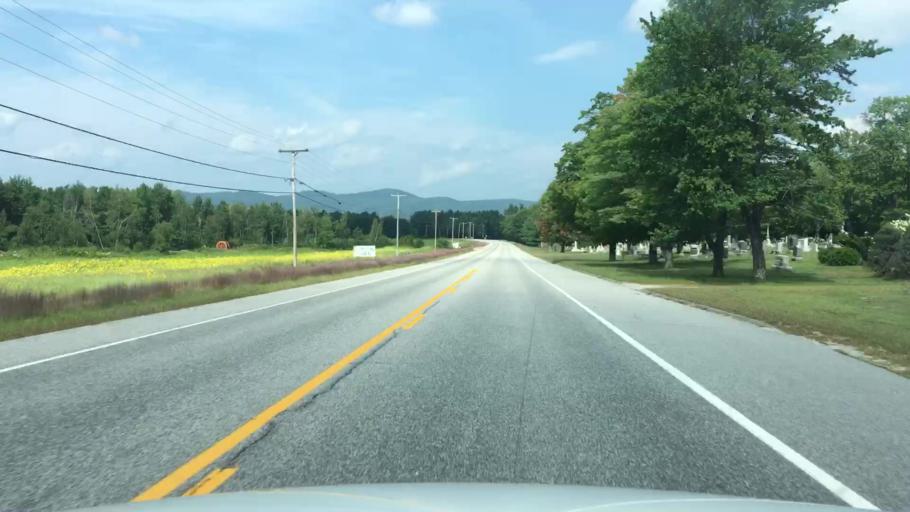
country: US
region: Maine
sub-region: Oxford County
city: Canton
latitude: 44.4611
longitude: -70.3207
